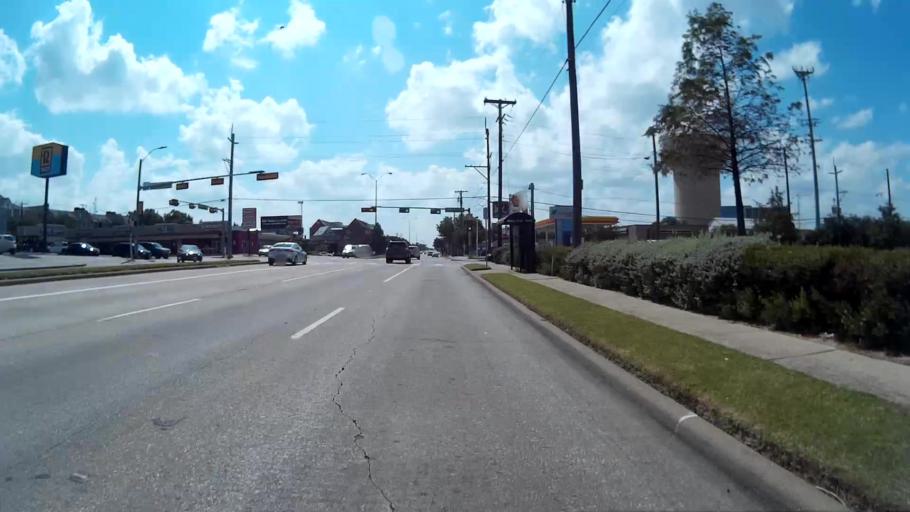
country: US
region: Texas
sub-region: Dallas County
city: Highland Park
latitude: 32.8461
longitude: -96.7702
